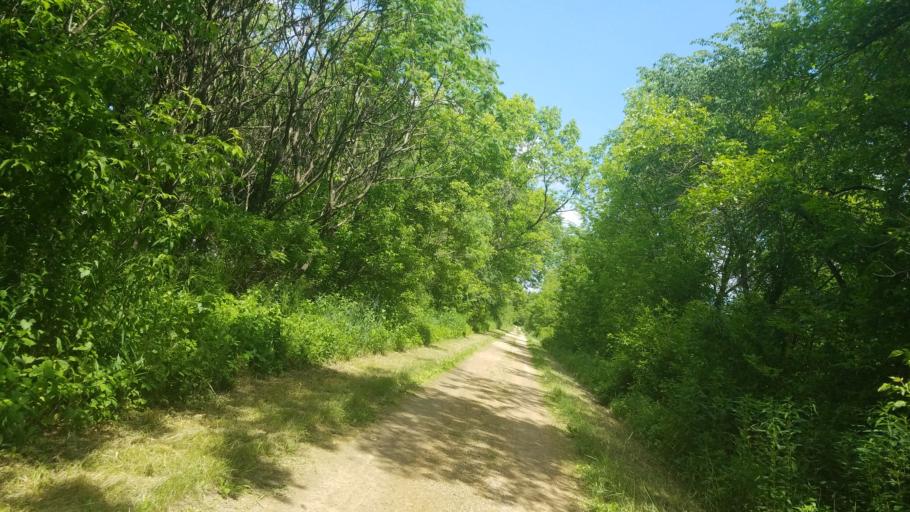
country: US
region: Wisconsin
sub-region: Dunn County
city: Menomonie
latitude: 44.7853
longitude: -91.9436
